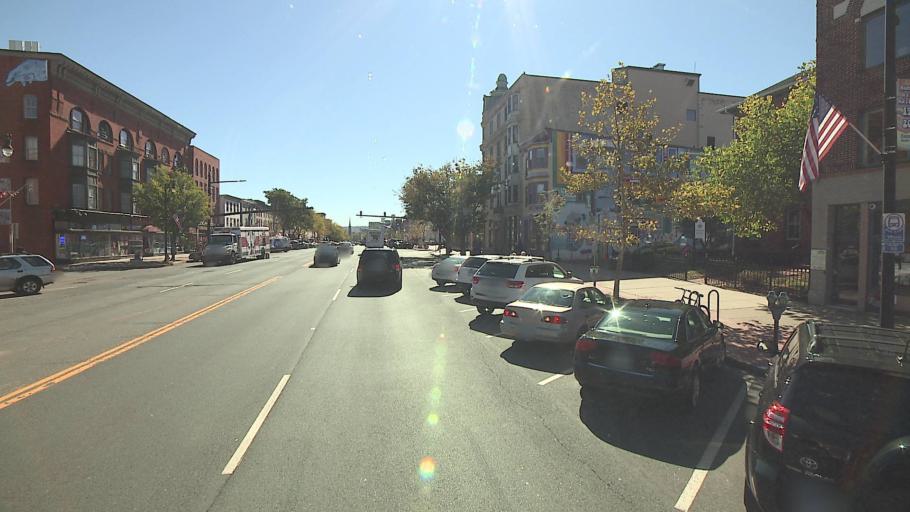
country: US
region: Connecticut
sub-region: Middlesex County
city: Middletown
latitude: 41.5647
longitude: -72.6523
